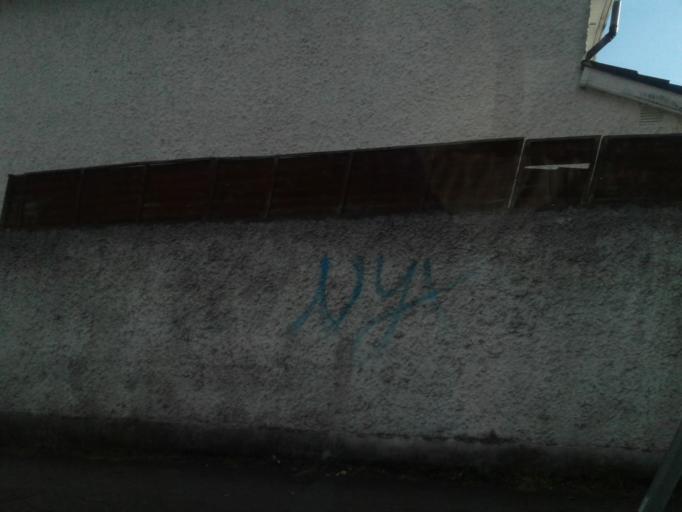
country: IE
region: Leinster
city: Marino
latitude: 53.3826
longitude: -6.2292
